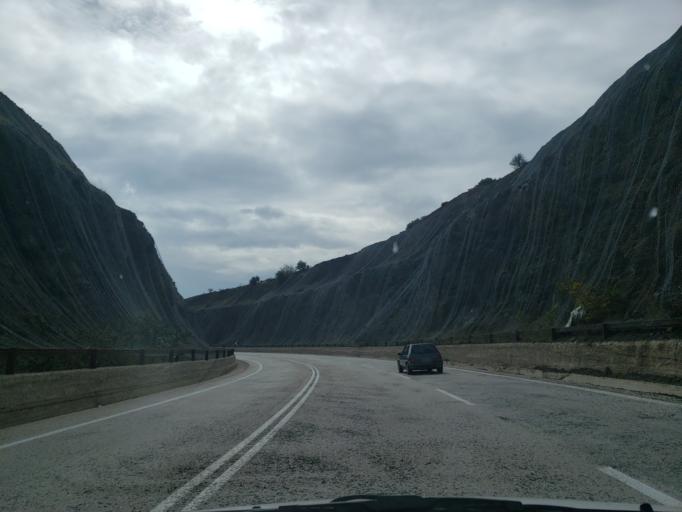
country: GR
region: Central Greece
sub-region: Nomos Fthiotidos
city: Stavros
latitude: 38.9908
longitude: 22.3726
